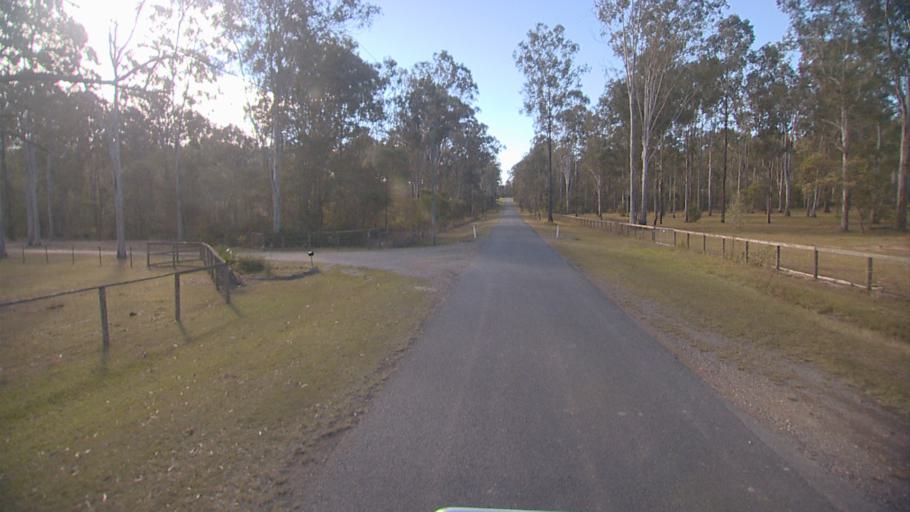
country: AU
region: Queensland
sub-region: Logan
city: Cedar Vale
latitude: -27.8248
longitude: 153.0628
